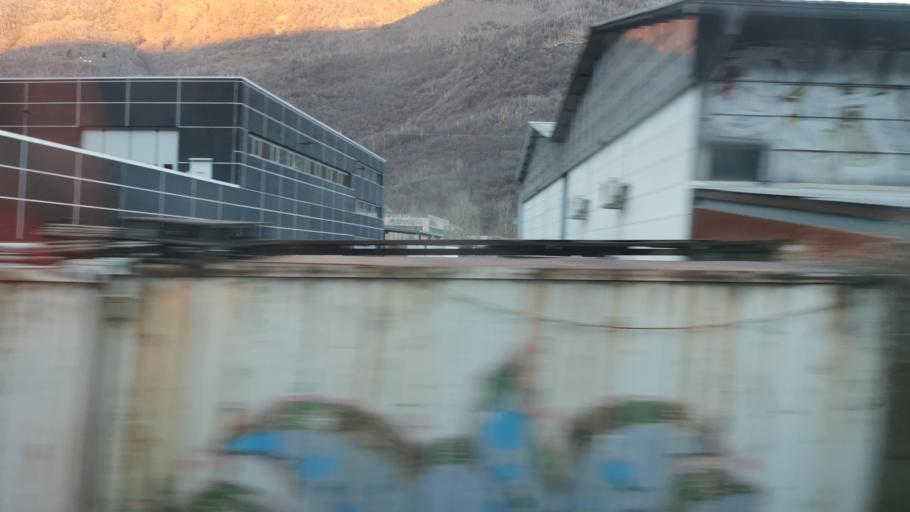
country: CH
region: Ticino
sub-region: Lugano District
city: Tesserete
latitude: 46.0984
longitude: 8.9316
